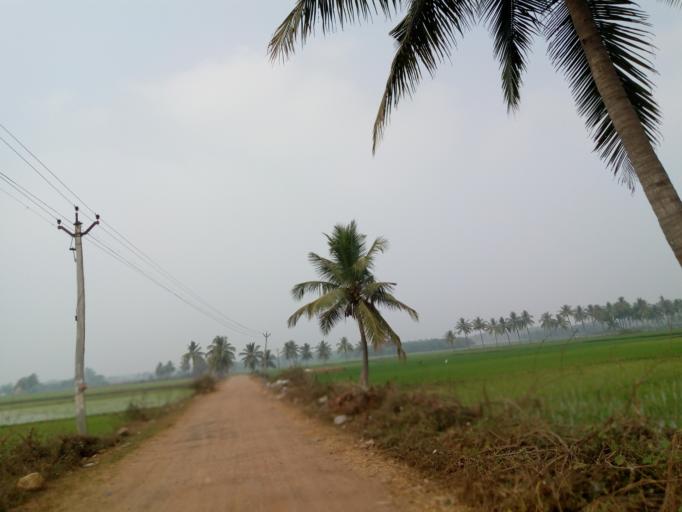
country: IN
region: Andhra Pradesh
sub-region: West Godavari
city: Tadepallegudem
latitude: 16.8628
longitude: 81.3143
